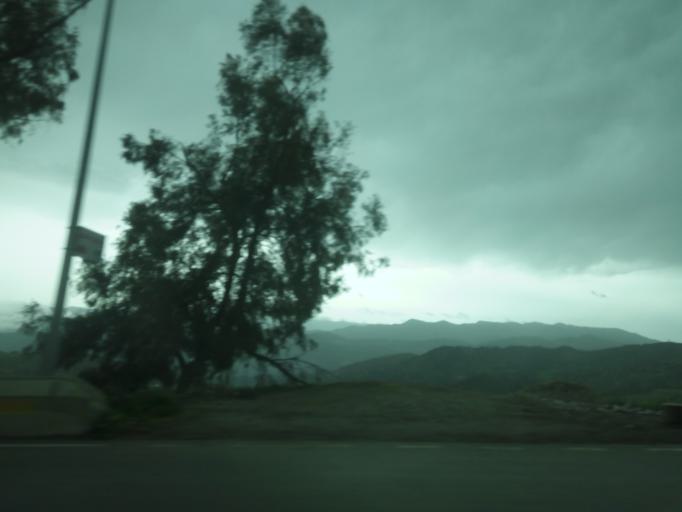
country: DZ
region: Medea
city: Medea
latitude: 36.2713
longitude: 2.7842
